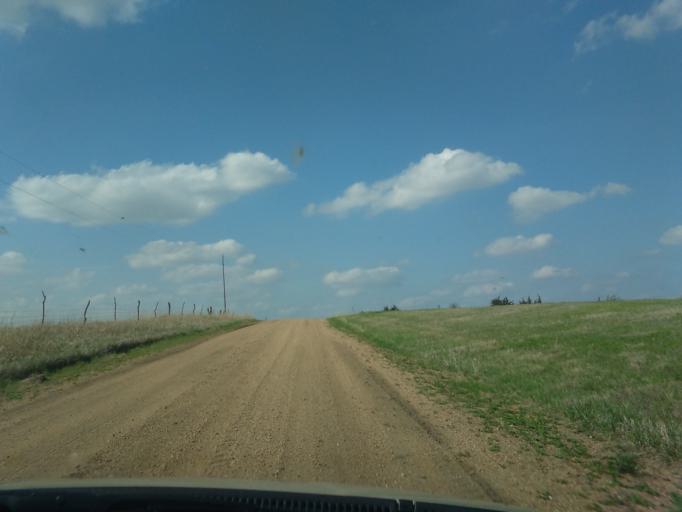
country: US
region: Nebraska
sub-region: Webster County
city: Red Cloud
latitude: 40.0240
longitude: -98.3492
